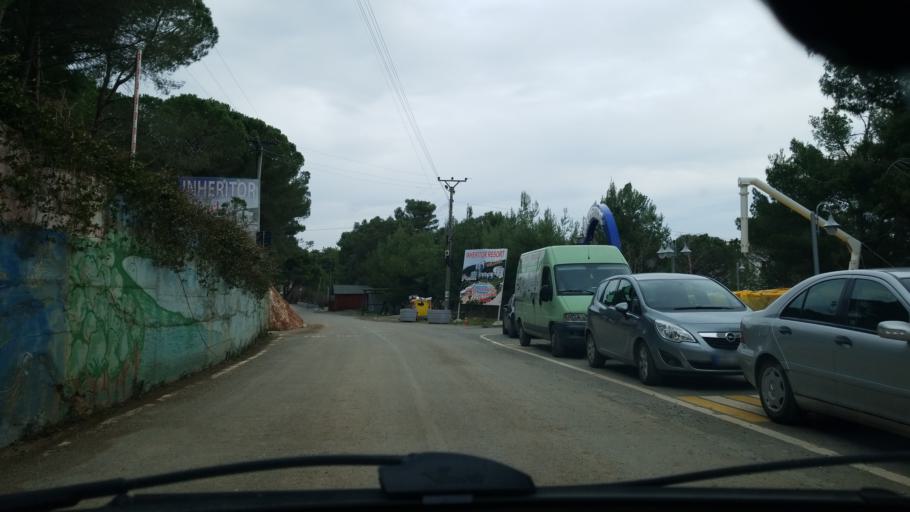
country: AL
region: Lezhe
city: Shengjin
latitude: 41.8130
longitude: 19.5753
